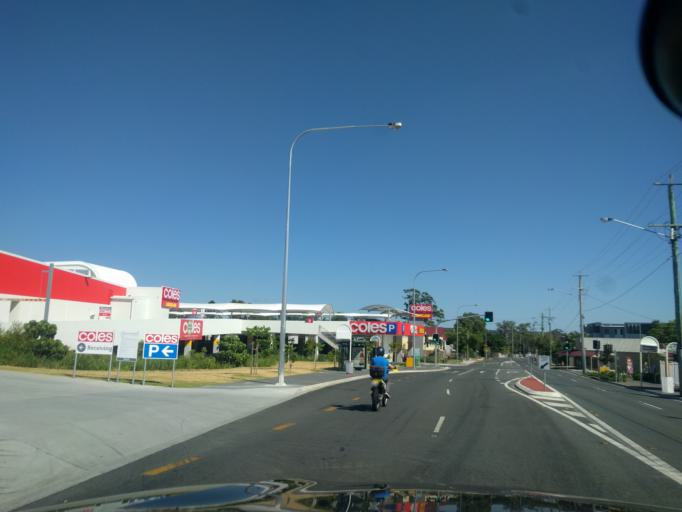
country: AU
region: Queensland
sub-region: Brisbane
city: Grange
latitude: -27.4242
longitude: 153.0005
